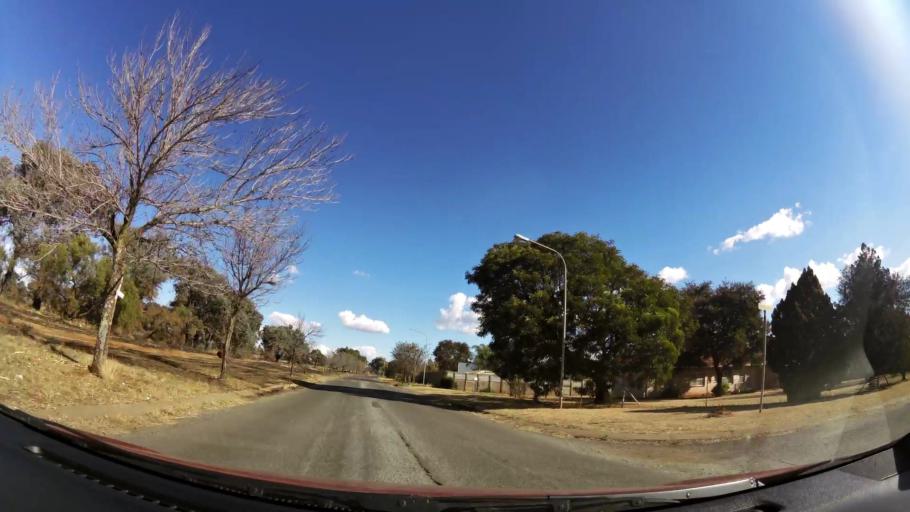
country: ZA
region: Gauteng
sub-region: West Rand District Municipality
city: Carletonville
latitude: -26.3638
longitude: 27.3715
